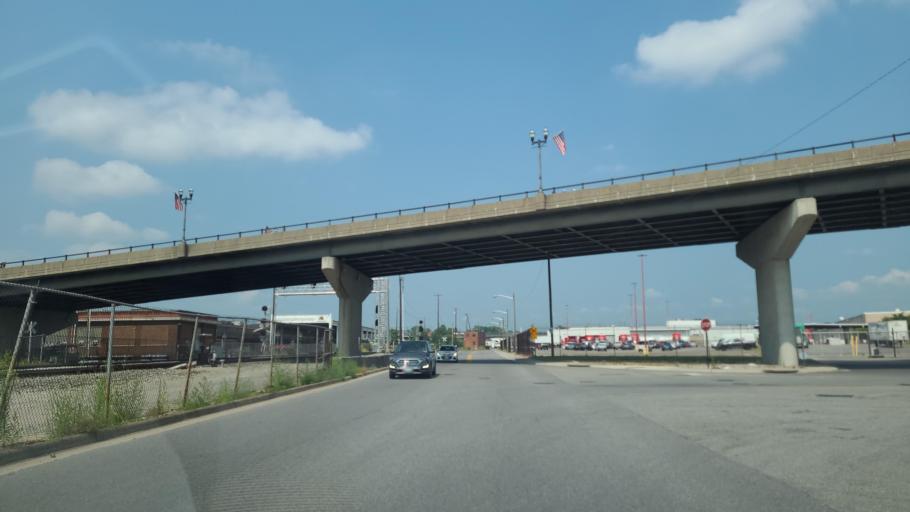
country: US
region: Virginia
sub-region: City of Roanoke
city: Roanoke
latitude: 37.2736
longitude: -79.9434
